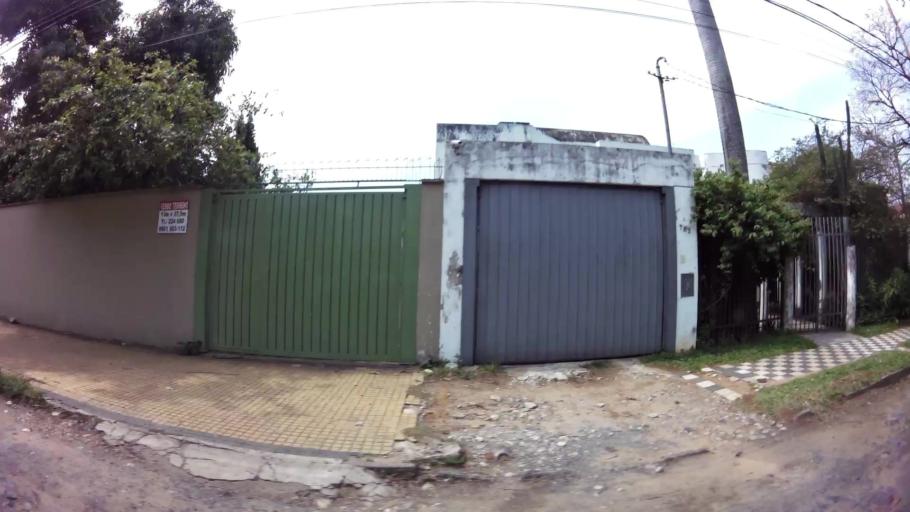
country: PY
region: Asuncion
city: Asuncion
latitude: -25.2748
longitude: -57.5761
